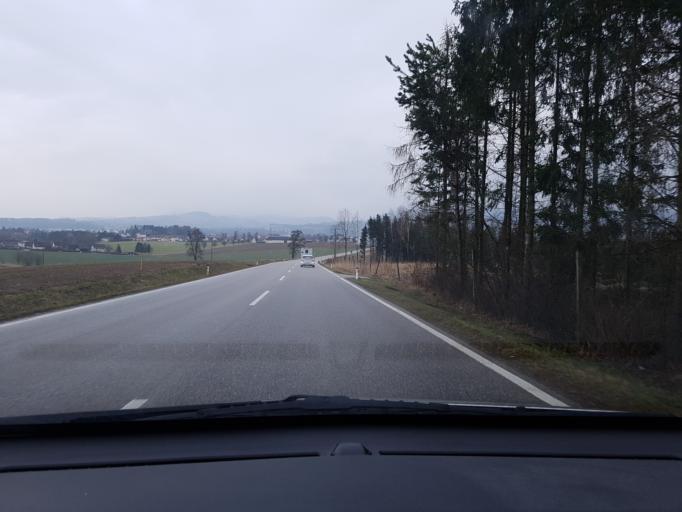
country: AT
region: Upper Austria
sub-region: Steyr Stadt
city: Steyr
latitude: 48.0561
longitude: 14.3889
